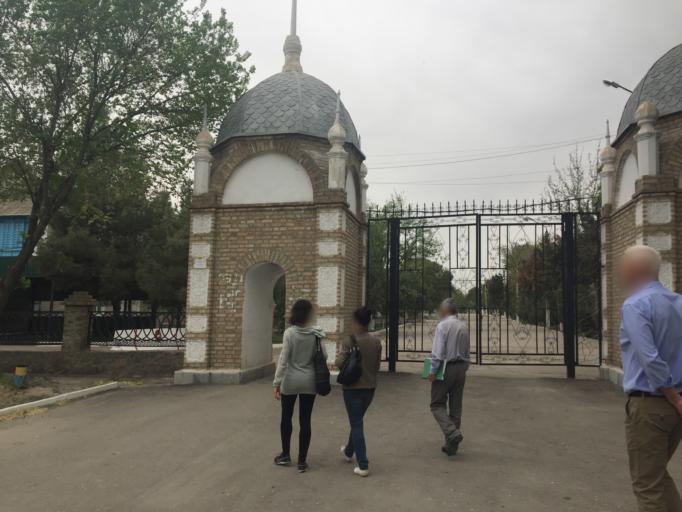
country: UZ
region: Bukhara
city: Kogon
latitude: 39.7227
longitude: 64.5453
